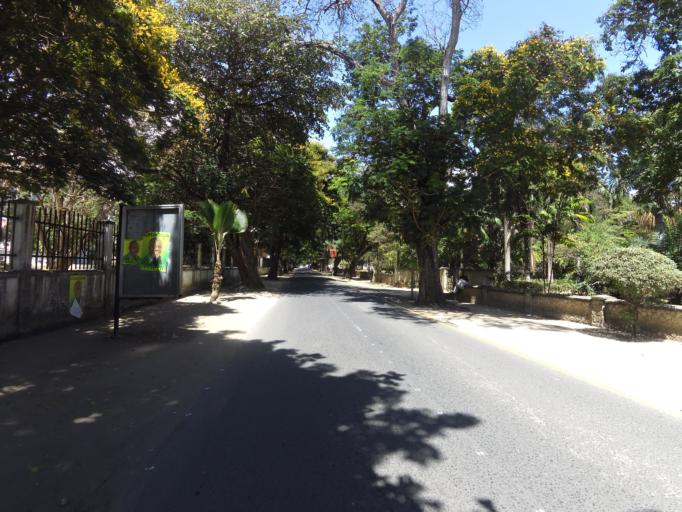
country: TZ
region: Dar es Salaam
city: Dar es Salaam
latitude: -6.8122
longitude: 39.2947
